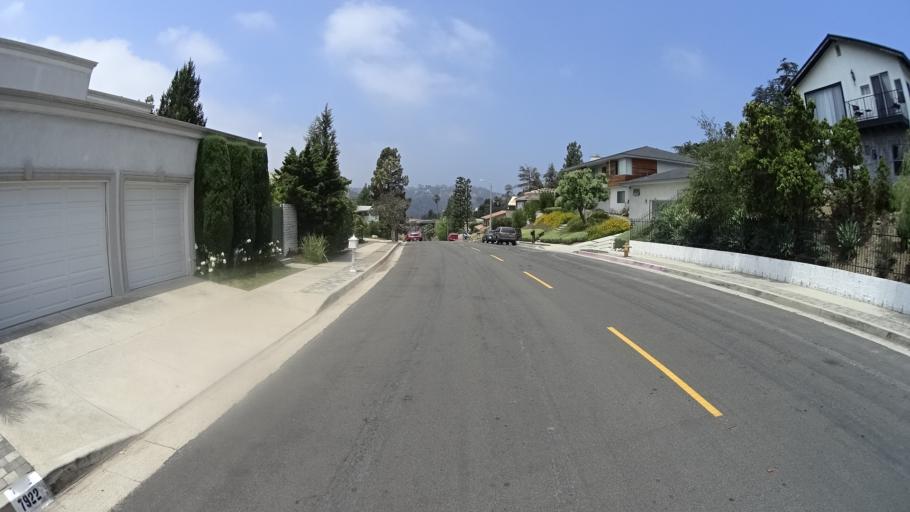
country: US
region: California
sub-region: Los Angeles County
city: West Hollywood
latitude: 34.1122
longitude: -118.3669
